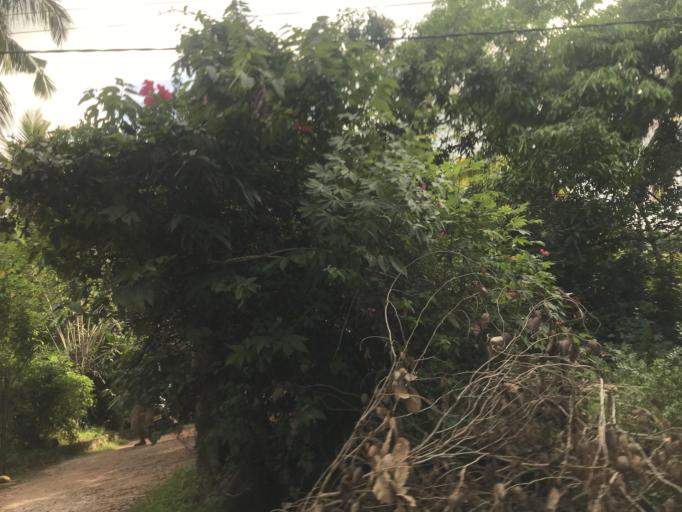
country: LK
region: Western
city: Gampaha
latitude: 7.0742
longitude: 79.9946
